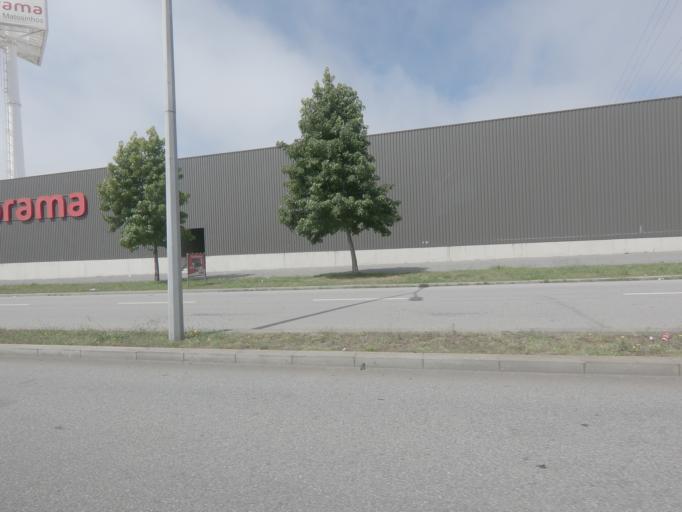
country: PT
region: Porto
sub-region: Matosinhos
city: Santa Cruz do Bispo
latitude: 41.2128
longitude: -8.6833
